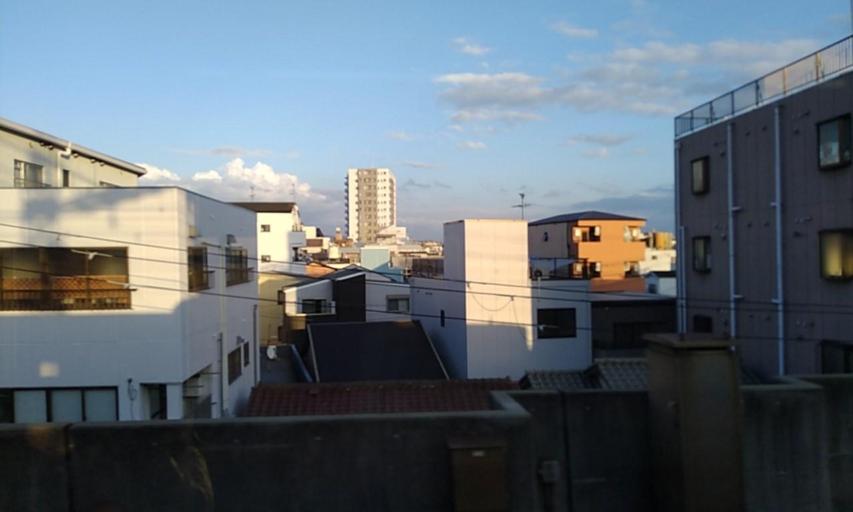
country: JP
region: Osaka
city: Sakai
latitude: 34.6323
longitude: 135.4955
